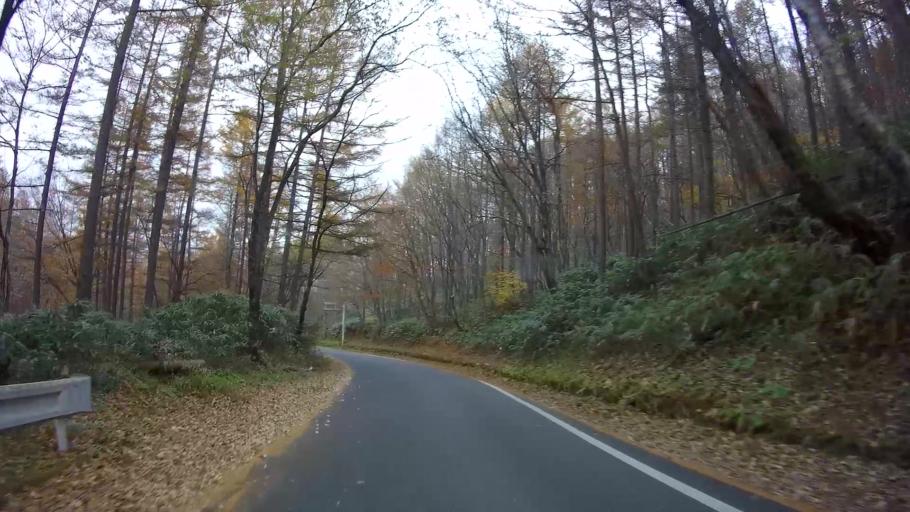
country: JP
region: Gunma
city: Nakanojomachi
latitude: 36.6733
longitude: 138.6689
